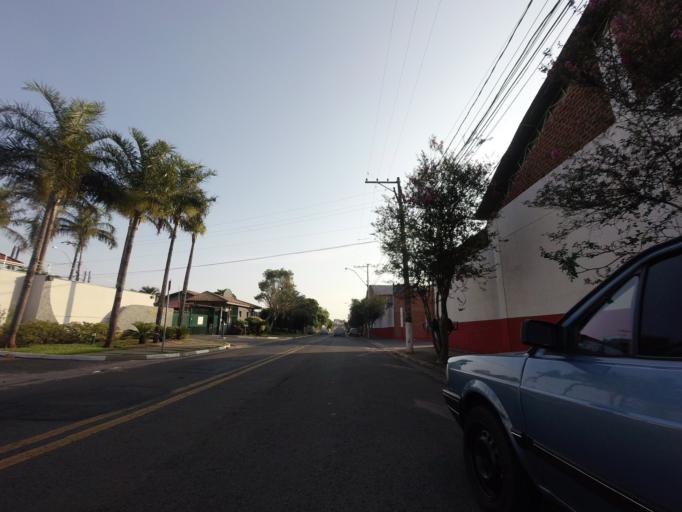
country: BR
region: Sao Paulo
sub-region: Piracicaba
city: Piracicaba
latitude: -22.7385
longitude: -47.6098
